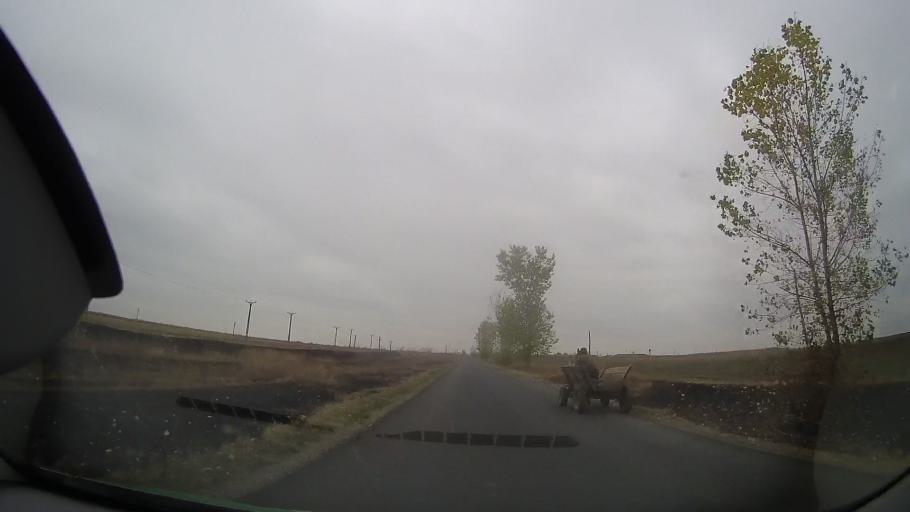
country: RO
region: Braila
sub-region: Comuna Ciocile
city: Ciocile
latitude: 44.8127
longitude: 27.2653
